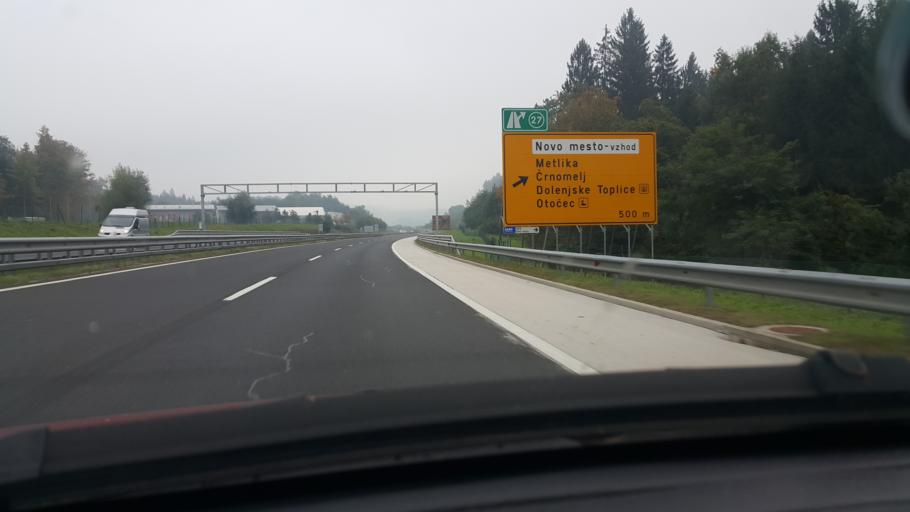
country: SI
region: Novo Mesto
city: Novo Mesto
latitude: 45.8351
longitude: 15.1700
